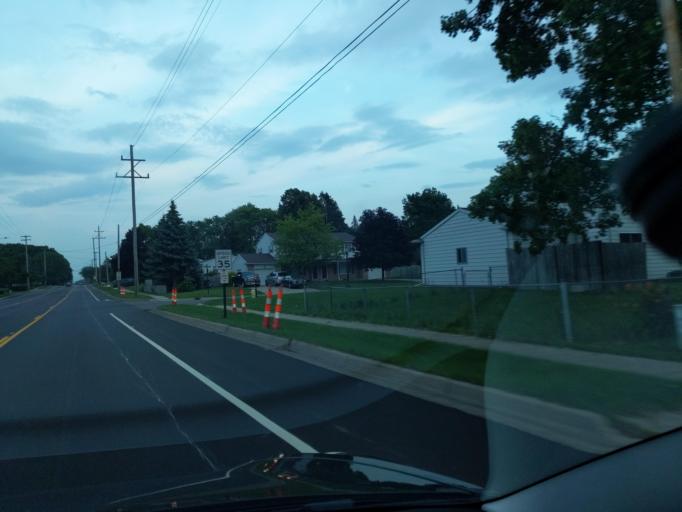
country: US
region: Michigan
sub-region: Eaton County
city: Waverly
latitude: 42.7338
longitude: -84.6305
